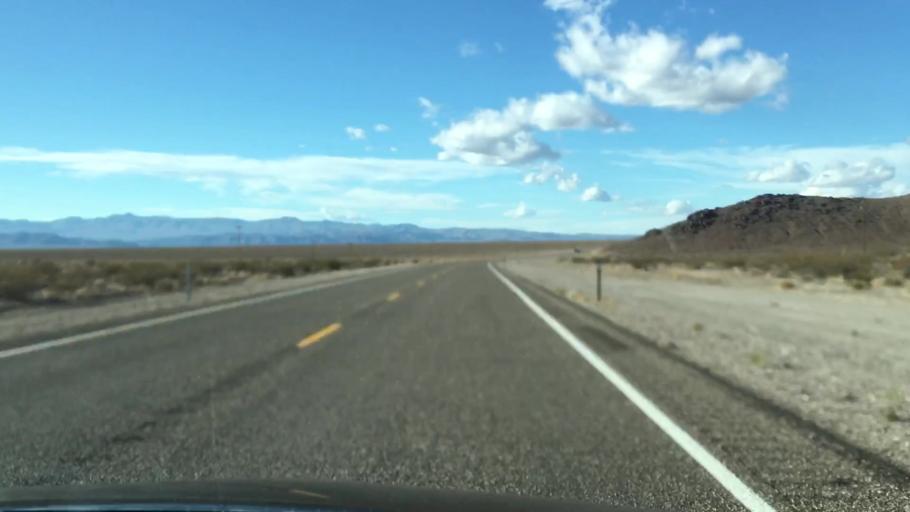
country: US
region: Nevada
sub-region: Nye County
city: Beatty
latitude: 37.1781
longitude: -116.9284
